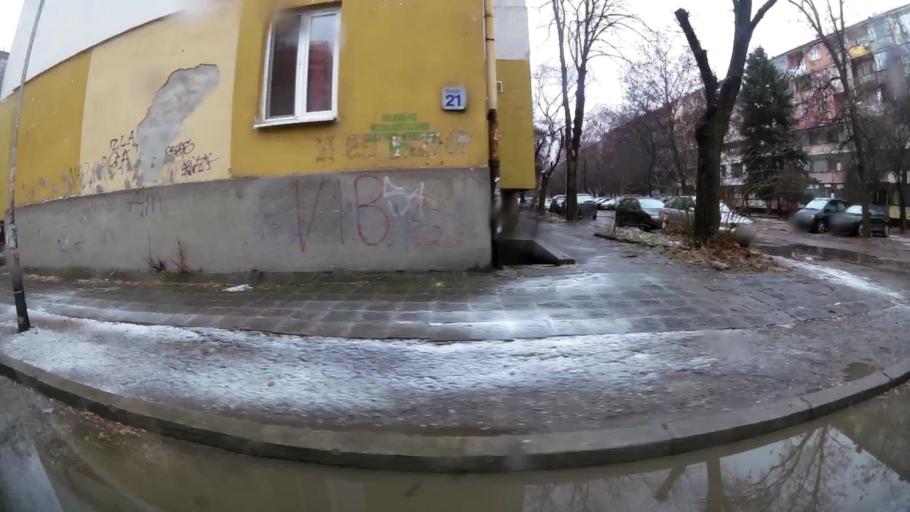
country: BG
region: Sofia-Capital
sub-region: Stolichna Obshtina
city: Sofia
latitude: 42.6702
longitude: 23.3953
